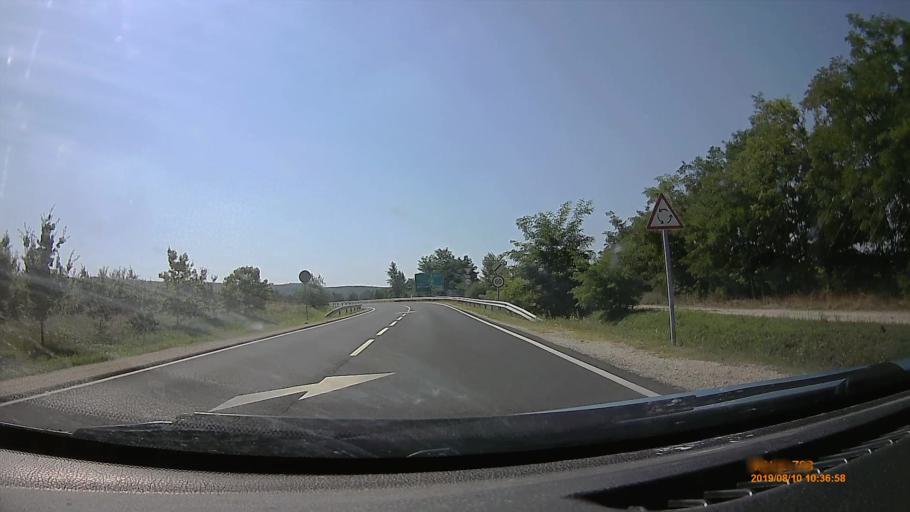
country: HU
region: Somogy
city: Balatonszarszo
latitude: 46.8223
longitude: 17.8543
